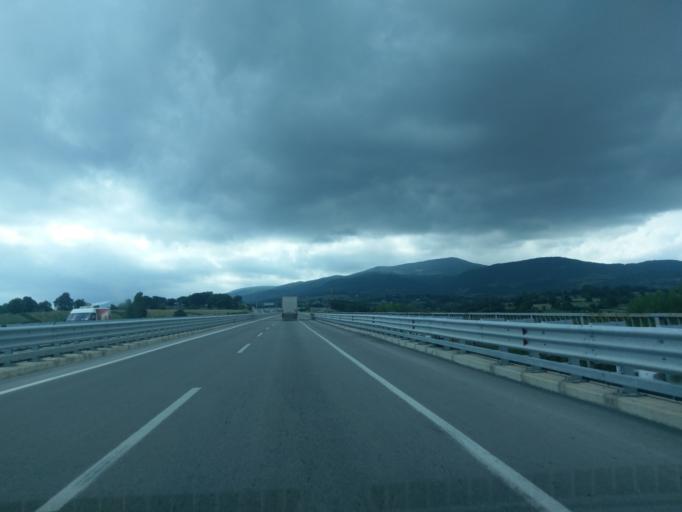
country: TR
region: Sinop
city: Gerze
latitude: 41.8195
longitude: 35.1673
